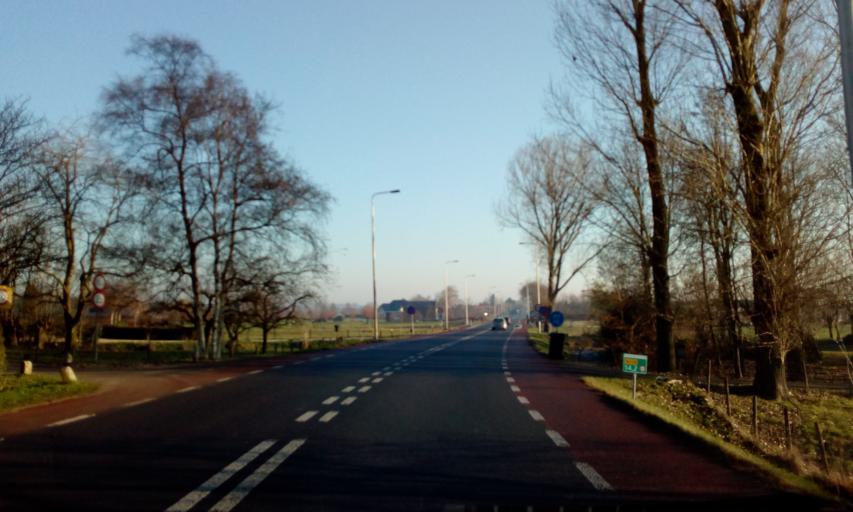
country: NL
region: Utrecht
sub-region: Gemeente Oudewater
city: Oudewater
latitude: 52.0235
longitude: 4.8993
